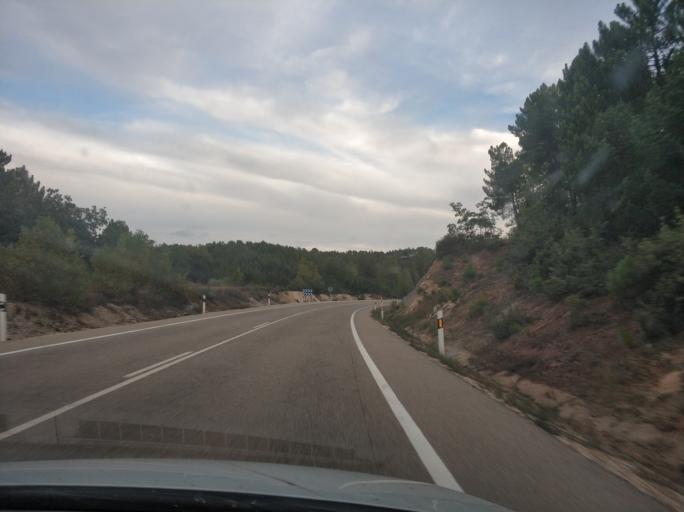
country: ES
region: Castille and Leon
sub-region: Provincia de Burgos
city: Pinilla de los Barruecos
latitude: 41.9135
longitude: -3.2764
